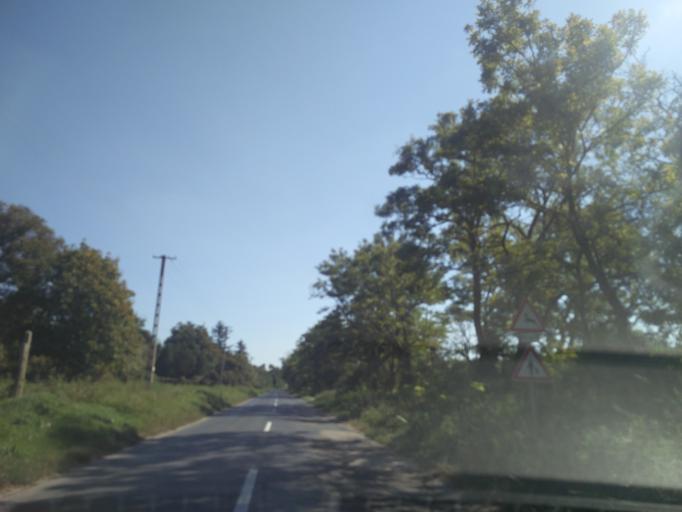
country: HU
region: Fejer
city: Lovasbereny
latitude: 47.2999
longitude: 18.5648
